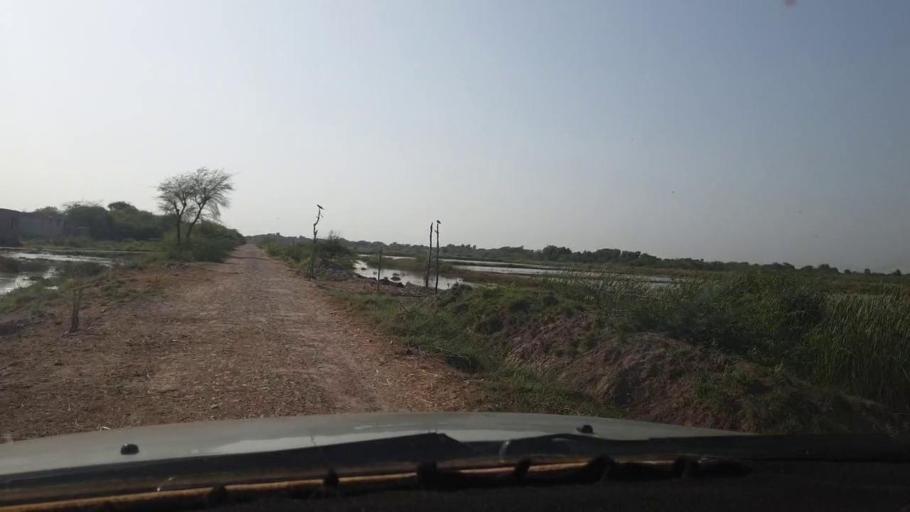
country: PK
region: Sindh
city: Chambar
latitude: 25.2648
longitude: 68.9310
